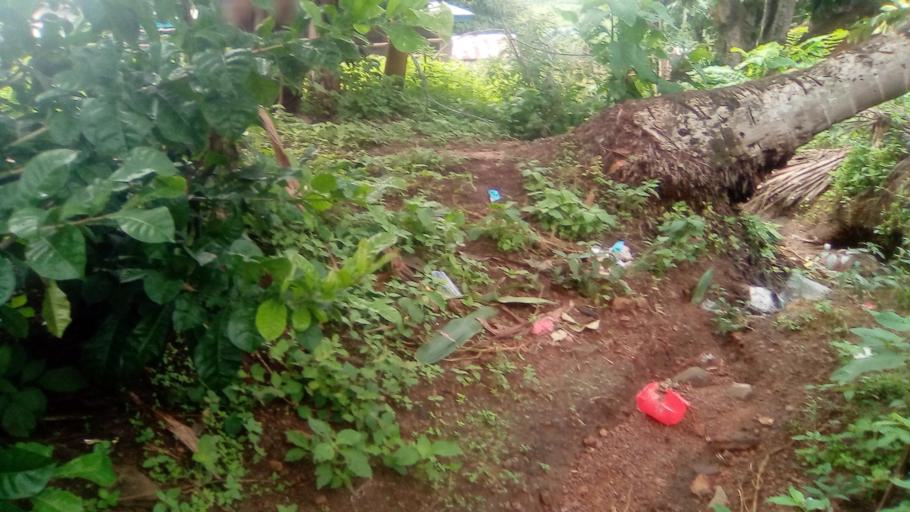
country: SL
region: Southern Province
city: Moyamba
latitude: 8.1553
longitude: -12.4284
